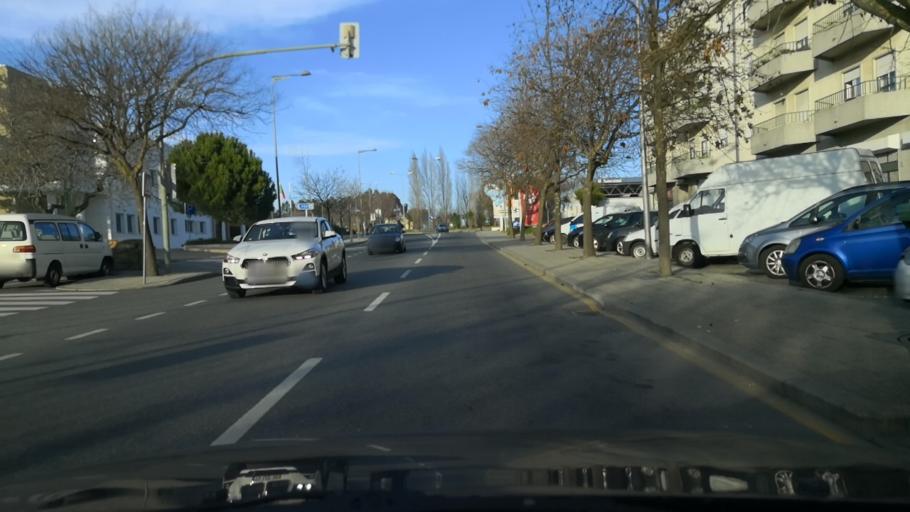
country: PT
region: Castelo Branco
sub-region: Castelo Branco
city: Castelo Branco
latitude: 39.8114
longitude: -7.5076
